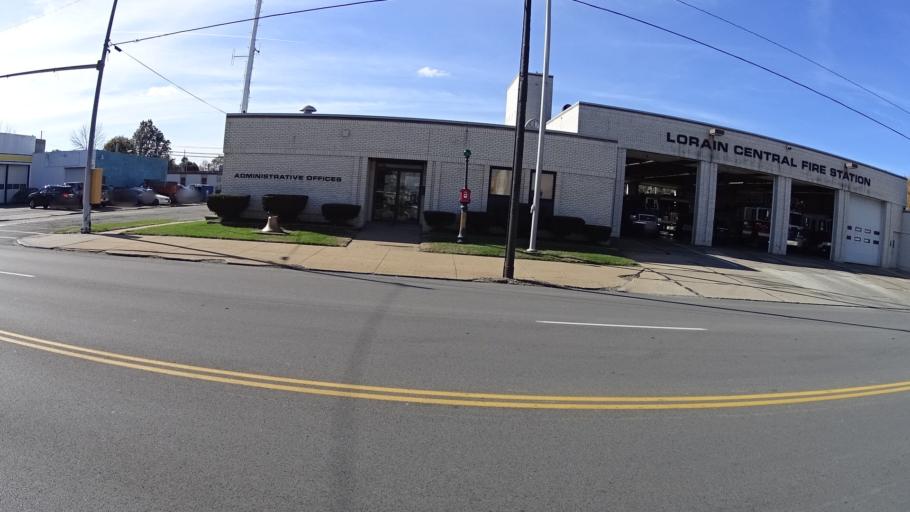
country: US
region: Ohio
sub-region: Lorain County
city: Lorain
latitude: 41.4589
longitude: -82.1691
